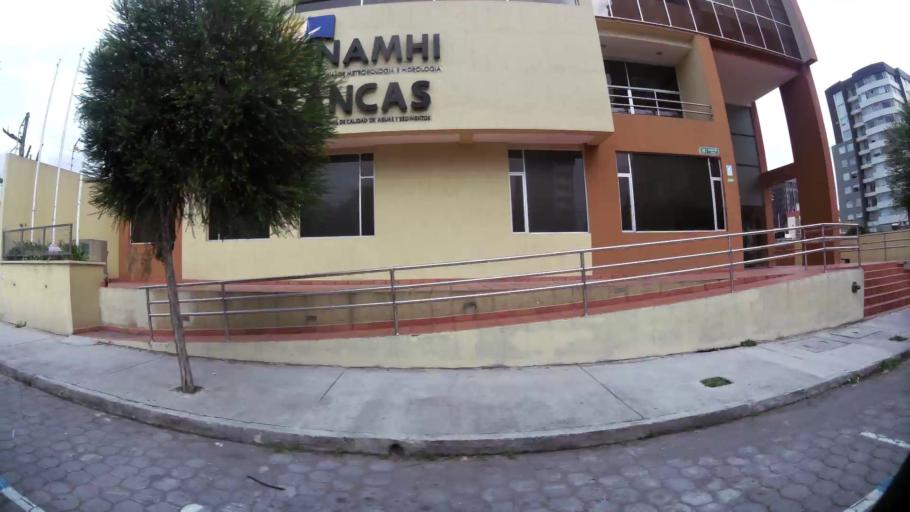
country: EC
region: Pichincha
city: Quito
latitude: -0.1779
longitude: -78.4874
